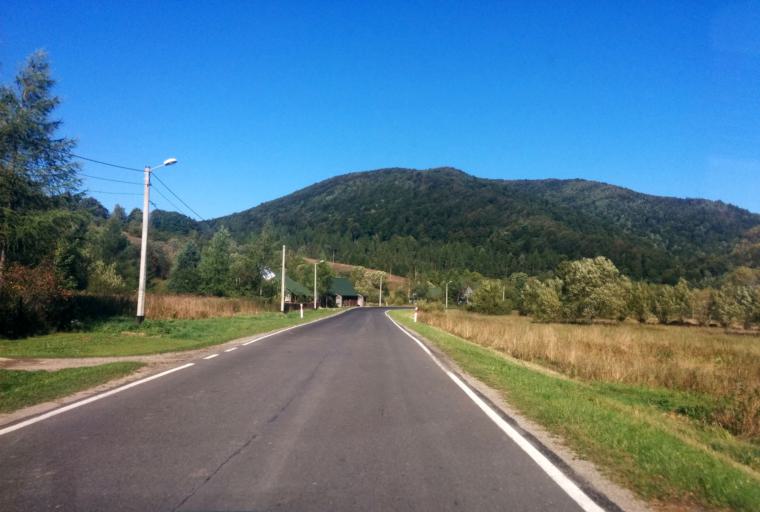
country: PL
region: Subcarpathian Voivodeship
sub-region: Powiat bieszczadzki
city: Lutowiska
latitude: 49.1362
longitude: 22.6688
